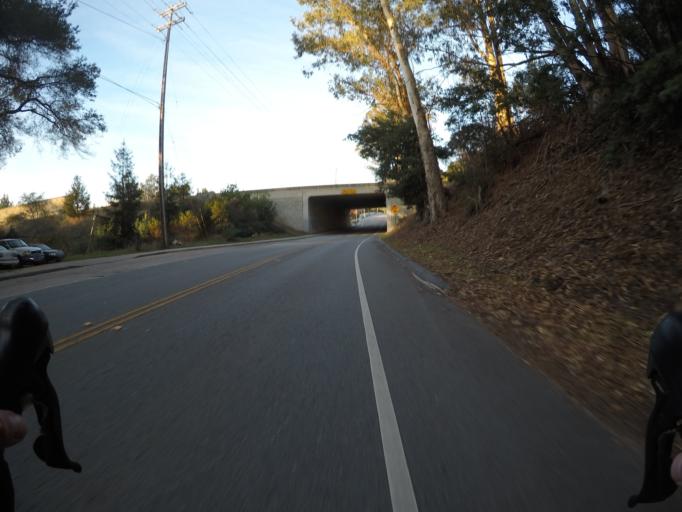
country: US
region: California
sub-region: Santa Cruz County
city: Pasatiempo
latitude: 36.9880
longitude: -122.0134
